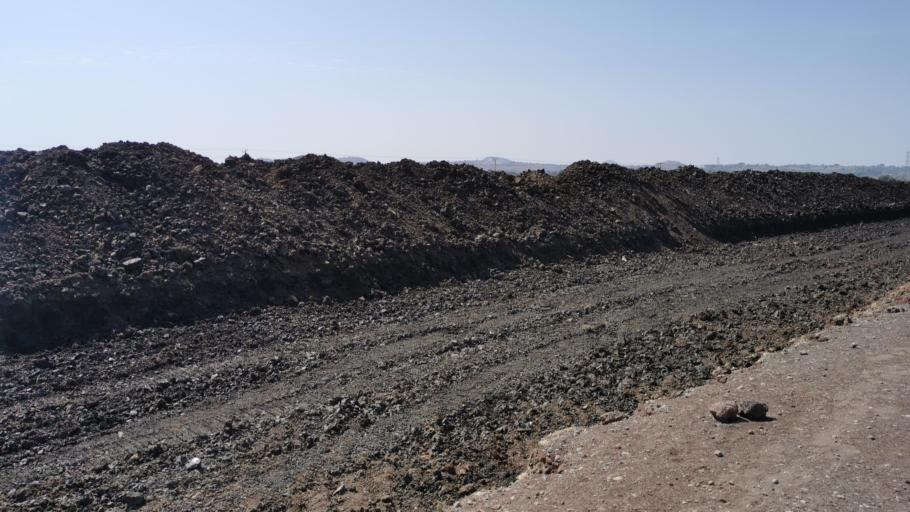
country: ET
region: Amhara
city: Bahir Dar
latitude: 11.8400
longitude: 37.0017
